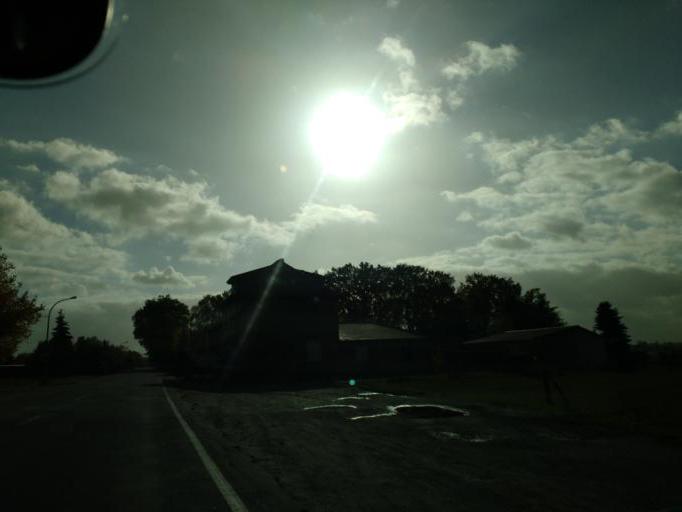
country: DE
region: Brandenburg
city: Spreenhagen
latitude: 52.3647
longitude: 13.8399
